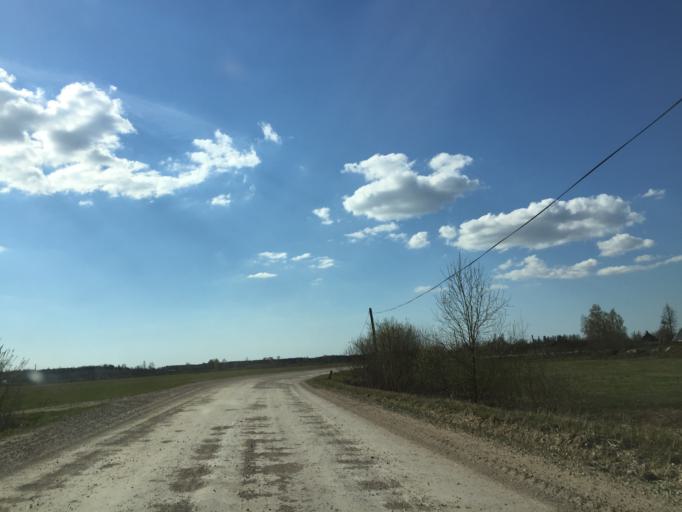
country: LV
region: Saulkrastu
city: Saulkrasti
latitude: 57.3461
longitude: 24.5813
